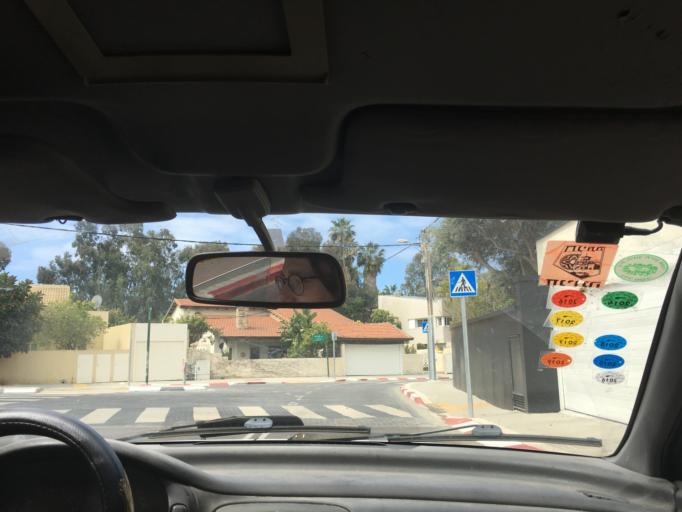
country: IL
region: Tel Aviv
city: Ramat HaSharon
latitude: 32.1424
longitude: 34.8288
